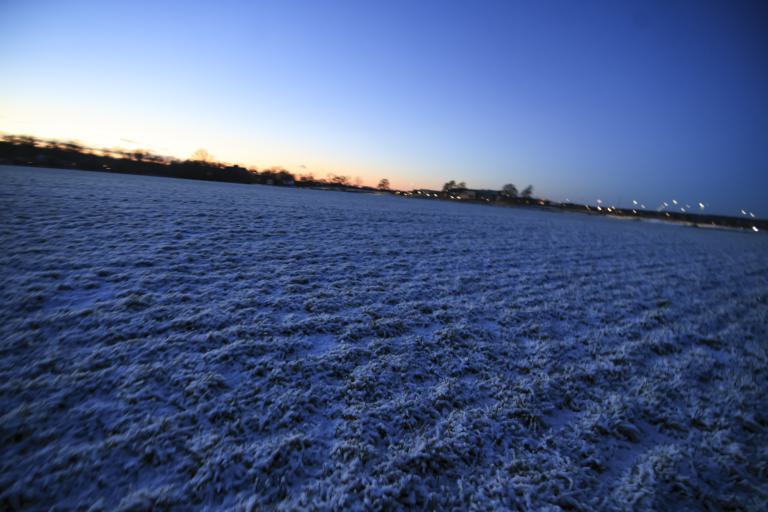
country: SE
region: Halland
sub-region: Varbergs Kommun
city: Varberg
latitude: 57.1355
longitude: 12.2800
